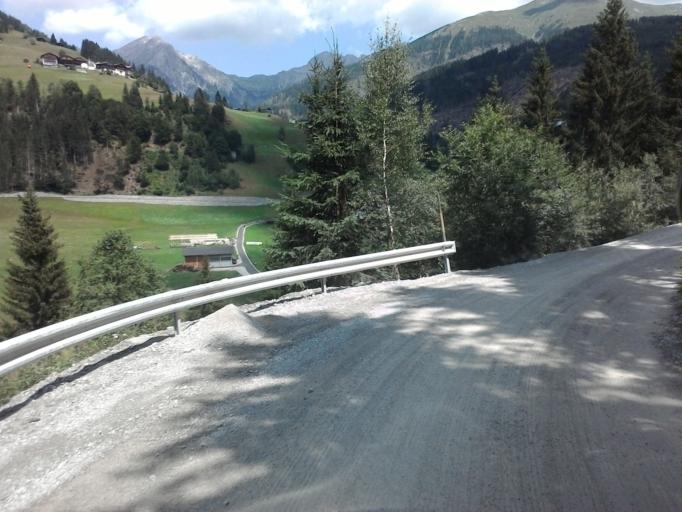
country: AT
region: Tyrol
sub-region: Politischer Bezirk Lienz
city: Untertilliach
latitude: 46.6986
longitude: 12.7709
